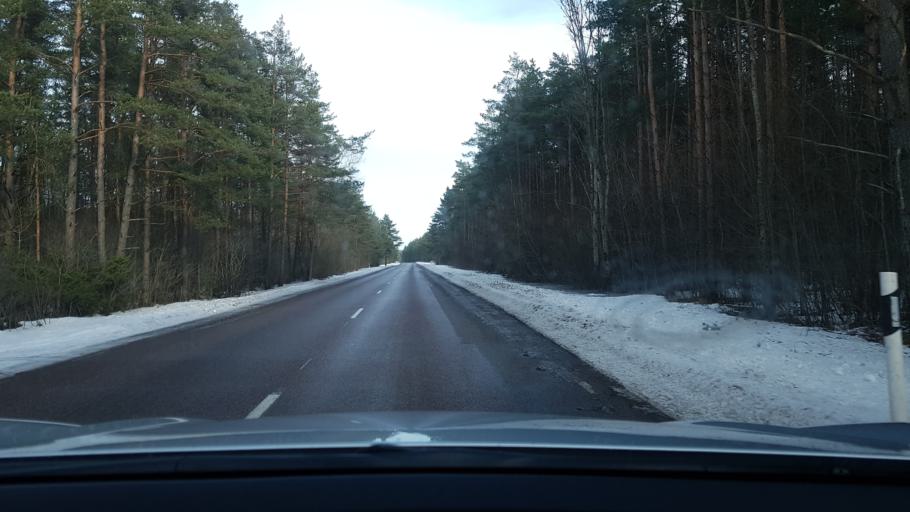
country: EE
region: Saare
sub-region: Kuressaare linn
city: Kuressaare
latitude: 58.3407
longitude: 22.5762
